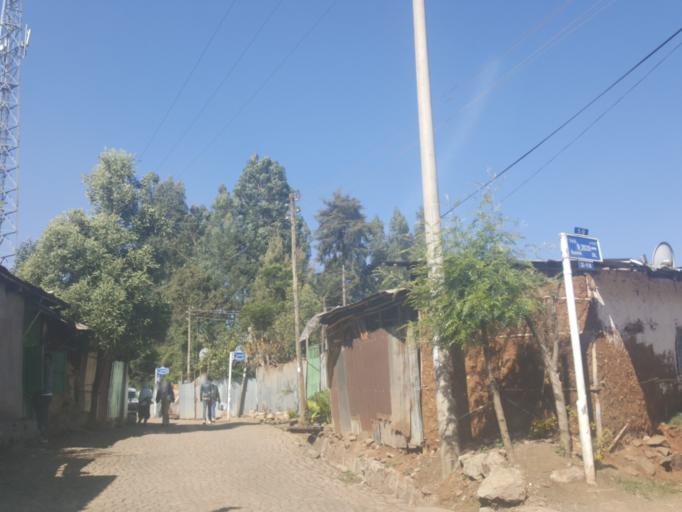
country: ET
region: Adis Abeba
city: Addis Ababa
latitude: 9.0618
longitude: 38.7270
